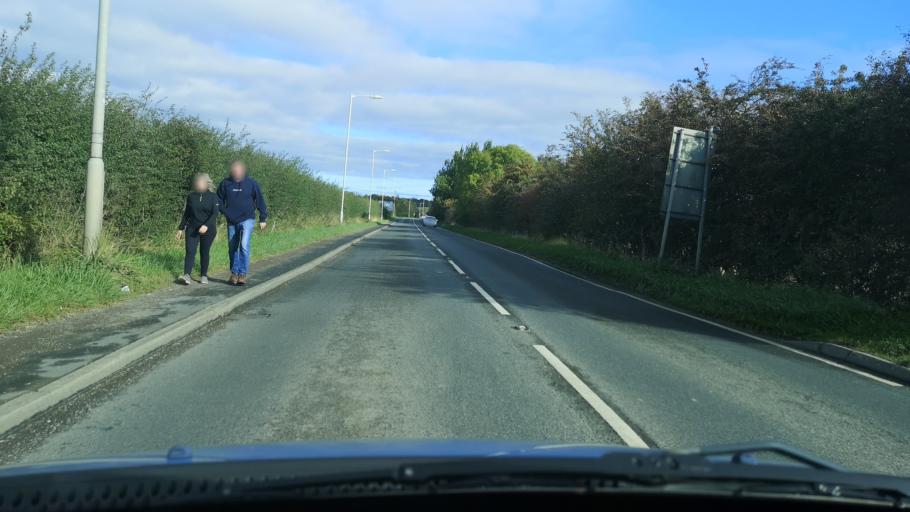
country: GB
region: England
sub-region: City and Borough of Wakefield
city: Featherstone
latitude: 53.6788
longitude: -1.3776
